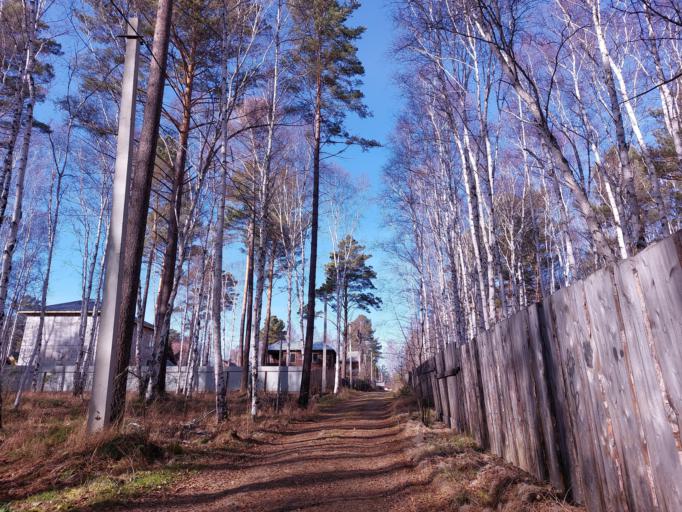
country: RU
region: Irkutsk
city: Pivovarikha
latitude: 52.1854
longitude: 104.4561
